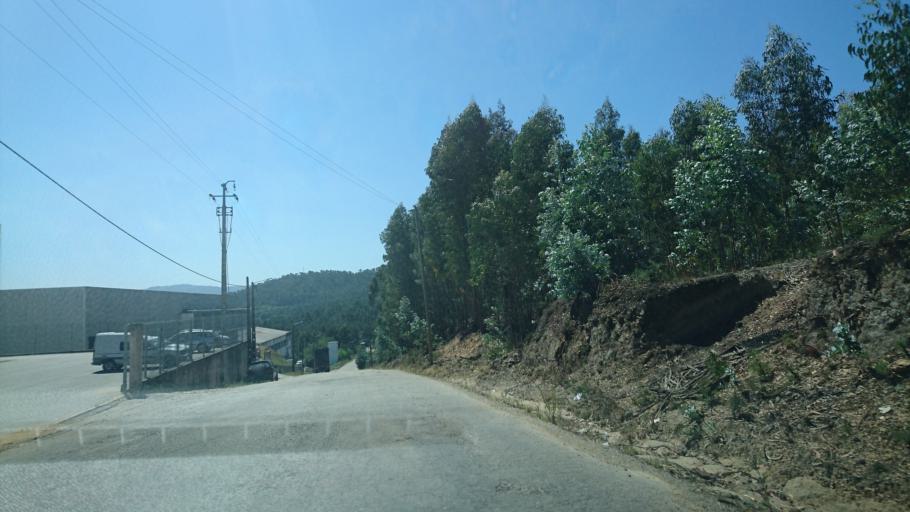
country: PT
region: Aveiro
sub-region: Oliveira de Azemeis
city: Vila Cha
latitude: 40.8837
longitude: -8.4296
